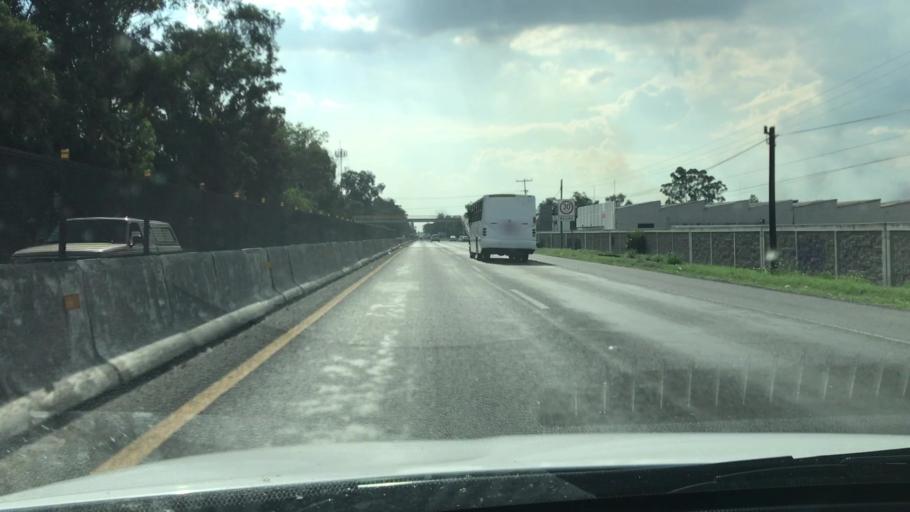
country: MX
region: Guanajuato
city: Valtierrilla
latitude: 20.5515
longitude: -101.1463
